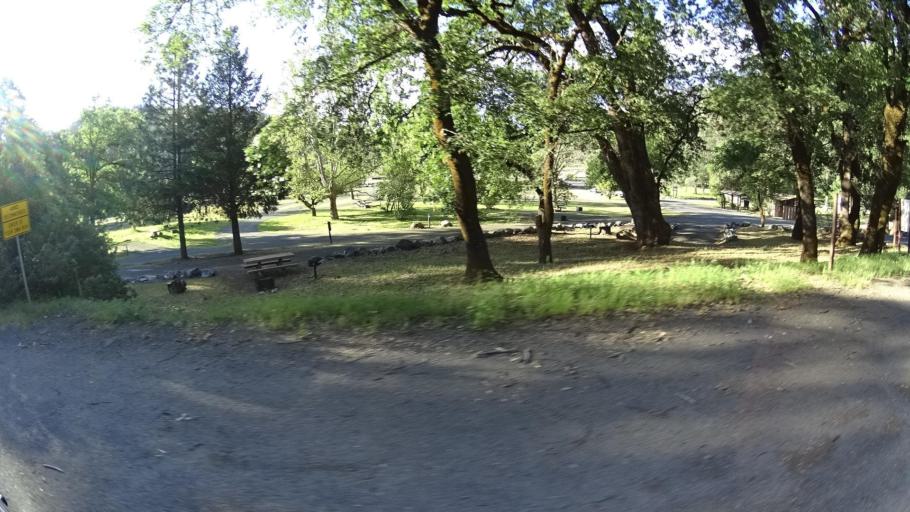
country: US
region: California
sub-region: Lake County
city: Upper Lake
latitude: 39.2535
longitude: -122.9517
